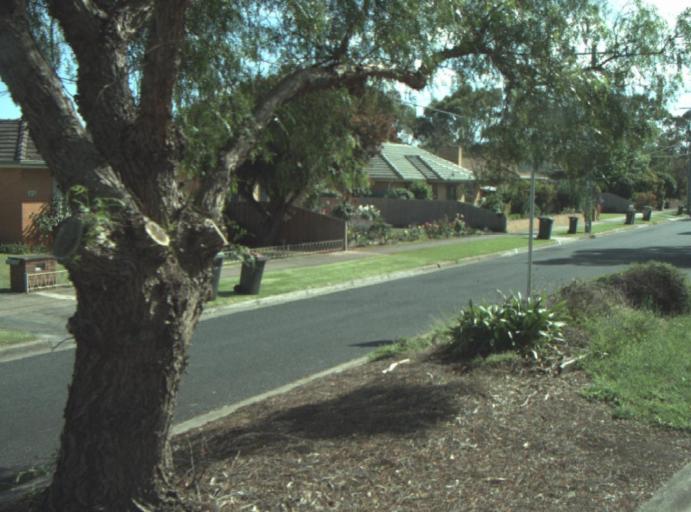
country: AU
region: Victoria
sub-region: Greater Geelong
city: Lara
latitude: -38.0204
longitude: 144.4010
